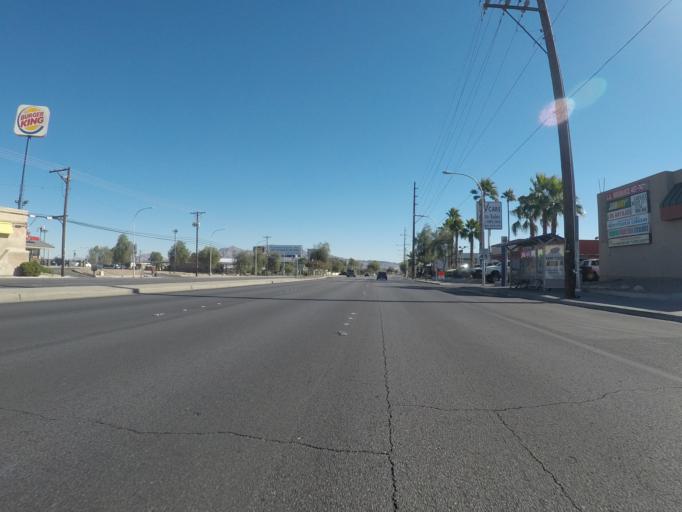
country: US
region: Nevada
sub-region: Clark County
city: Winchester
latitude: 36.1442
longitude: -115.1183
